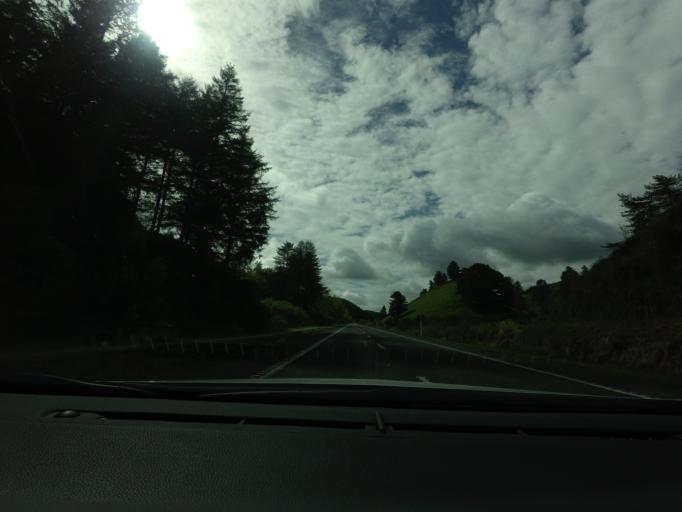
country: NZ
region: Bay of Plenty
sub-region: Rotorua District
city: Rotorua
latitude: -38.2163
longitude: 176.2749
